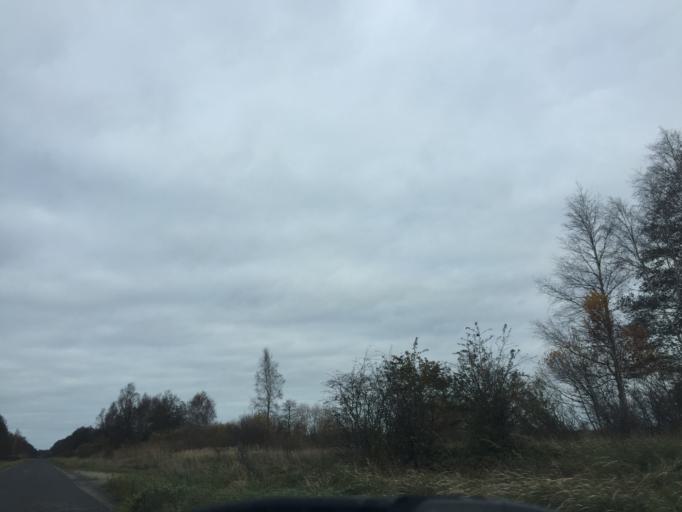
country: LV
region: Liepaja
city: Vec-Liepaja
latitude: 56.5571
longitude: 21.0622
